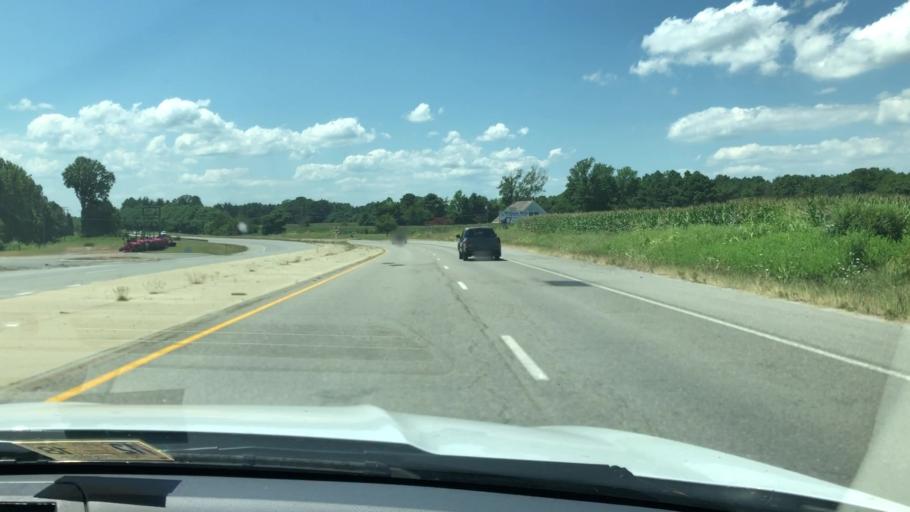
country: US
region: Virginia
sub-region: Middlesex County
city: Saluda
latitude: 37.6004
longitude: -76.5140
